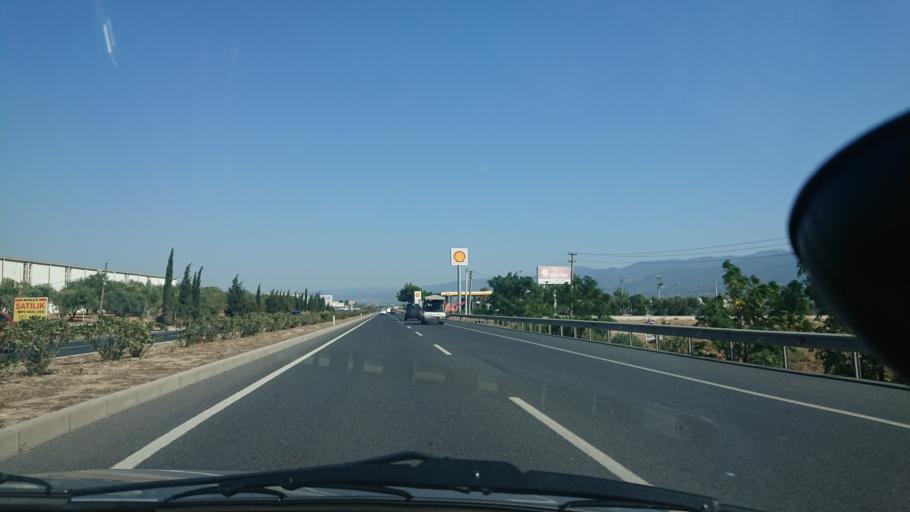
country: TR
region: Izmir
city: Kemalpasa
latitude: 38.4507
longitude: 27.4880
